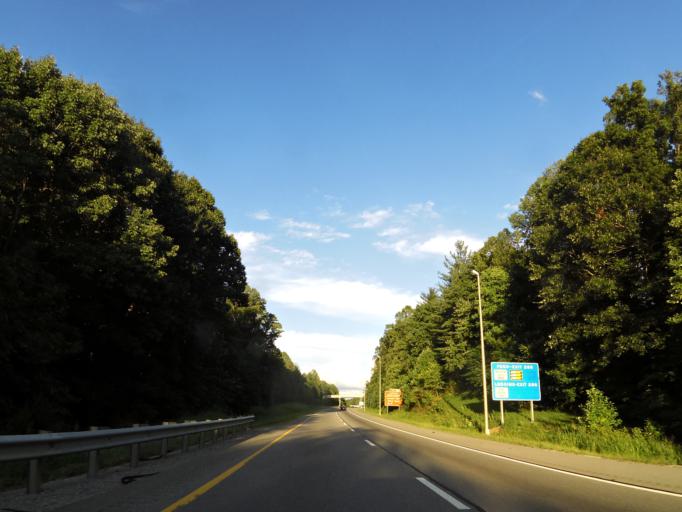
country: US
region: Tennessee
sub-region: Putnam County
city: Cookeville
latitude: 36.1372
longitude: -85.4918
